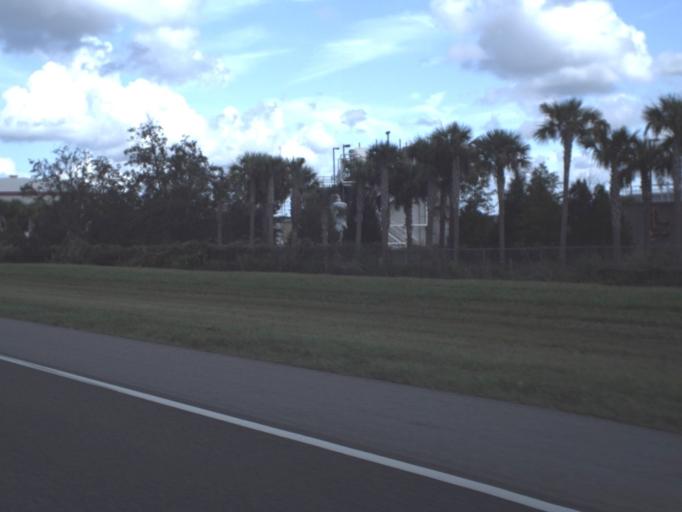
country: US
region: Florida
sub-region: Sarasota County
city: Nokomis
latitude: 27.1310
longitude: -82.4021
